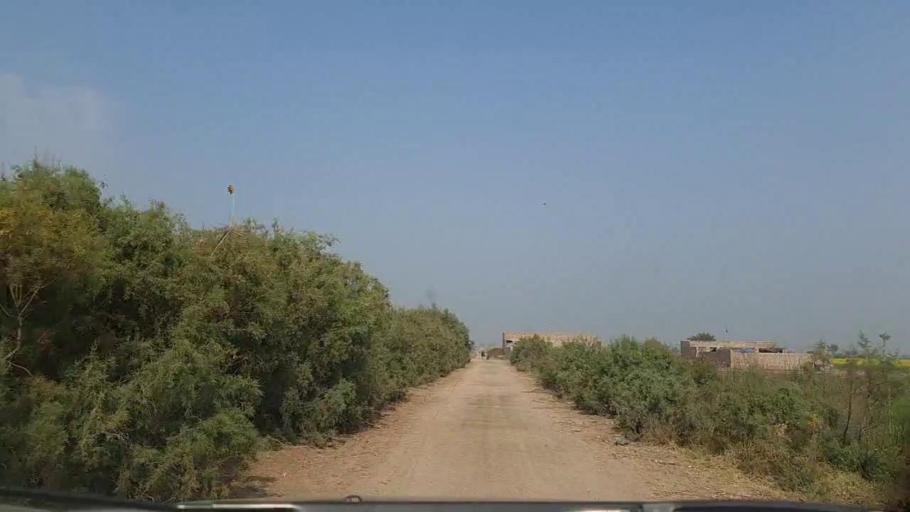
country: PK
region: Sindh
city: Sanghar
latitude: 26.0789
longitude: 68.9503
